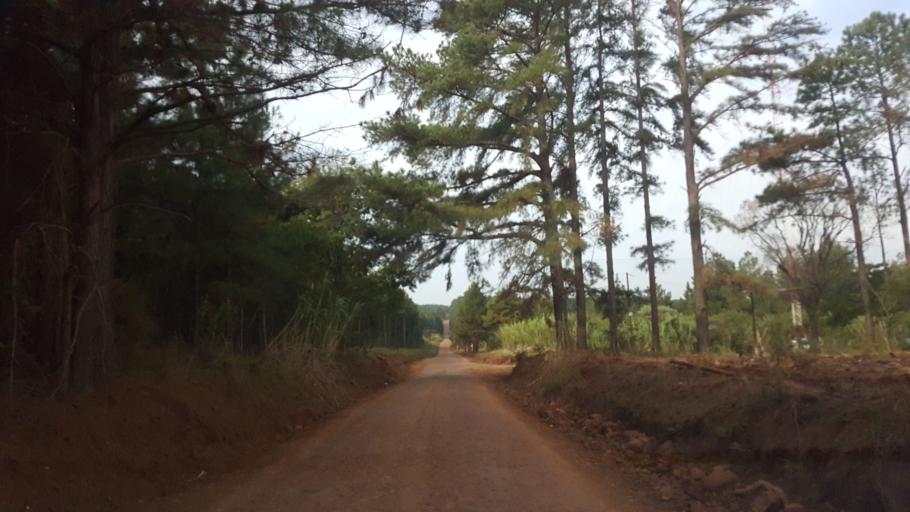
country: AR
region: Misiones
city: Capiovi
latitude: -26.9252
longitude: -55.1162
